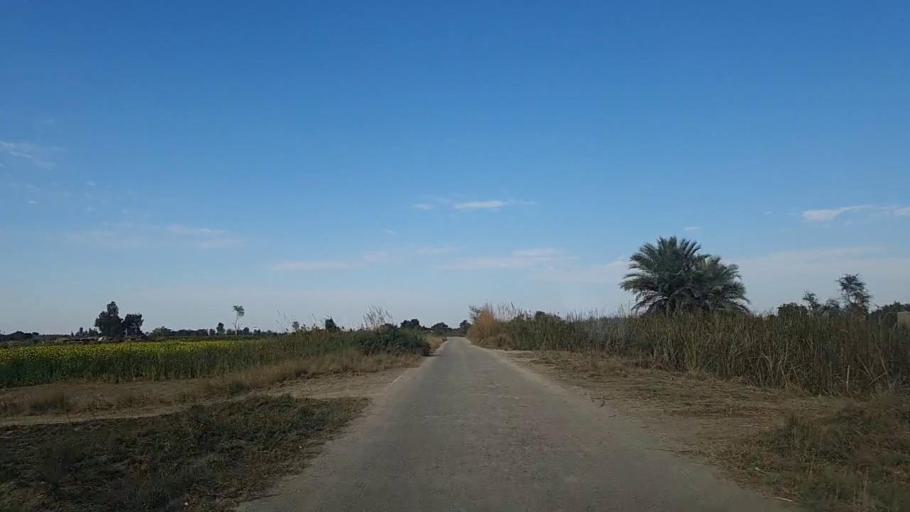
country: PK
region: Sindh
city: Khadro
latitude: 26.2863
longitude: 68.8199
